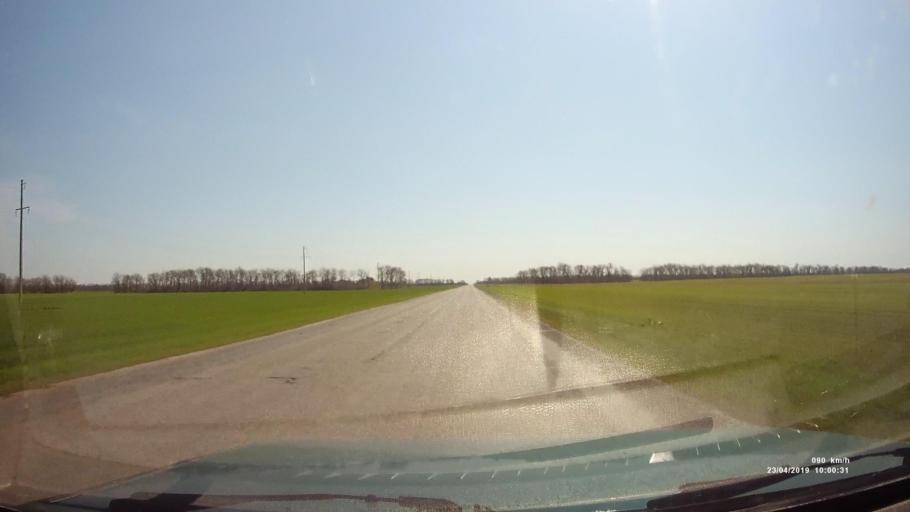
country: RU
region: Rostov
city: Sovetskoye
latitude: 46.7704
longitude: 42.1342
